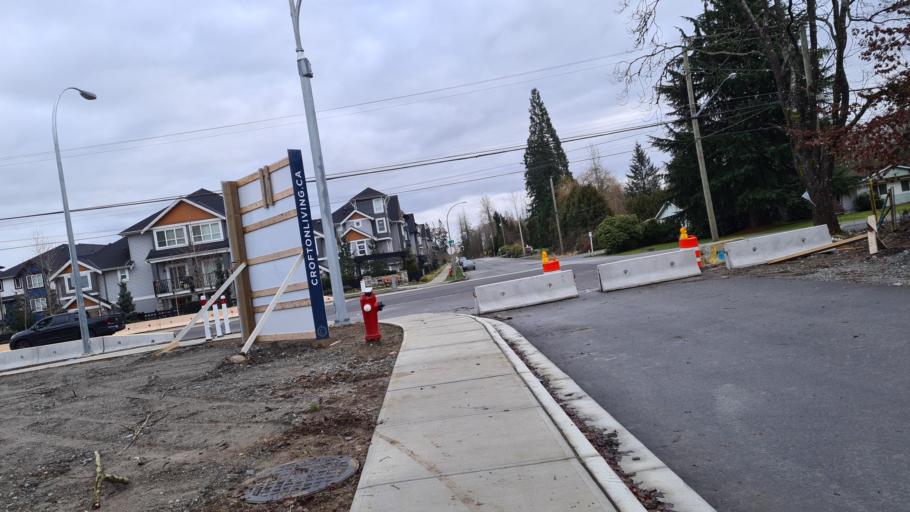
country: CA
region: British Columbia
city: Walnut Grove
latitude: 49.1409
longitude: -122.6463
